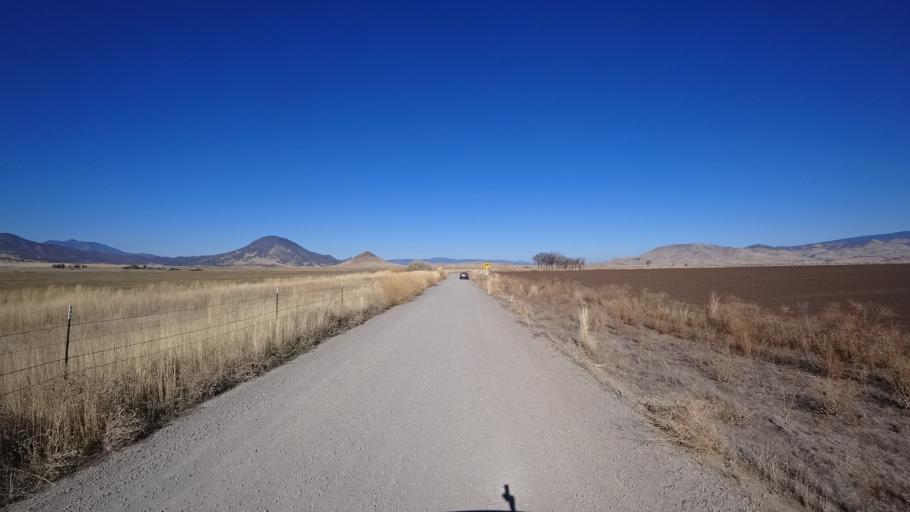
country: US
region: California
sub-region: Siskiyou County
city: Montague
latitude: 41.7869
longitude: -122.4613
